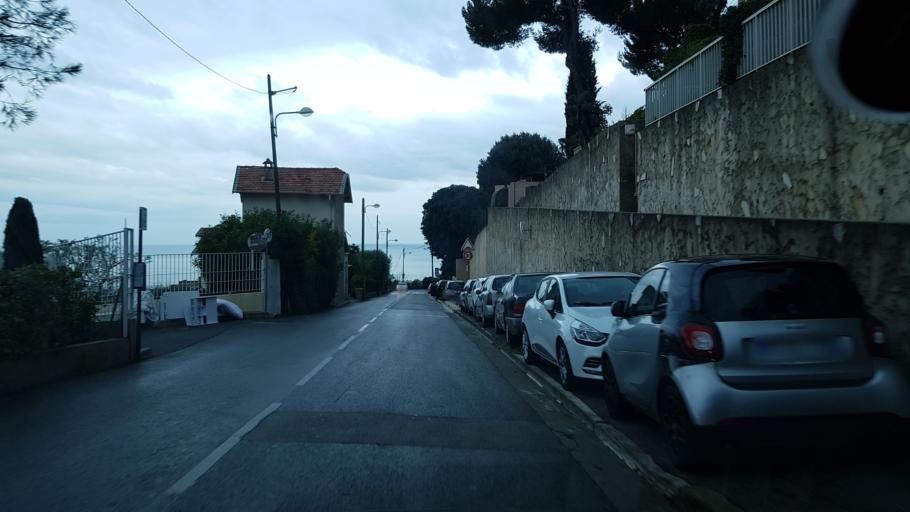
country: FR
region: Provence-Alpes-Cote d'Azur
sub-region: Departement des Alpes-Maritimes
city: Nice
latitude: 43.6970
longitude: 7.2388
